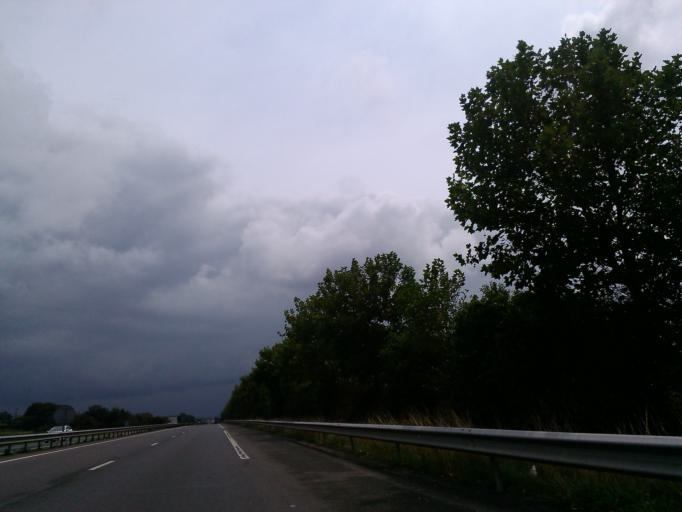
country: FR
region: Poitou-Charentes
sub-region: Departement de la Charente
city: Saint-Brice
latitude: 45.6794
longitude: -0.2851
